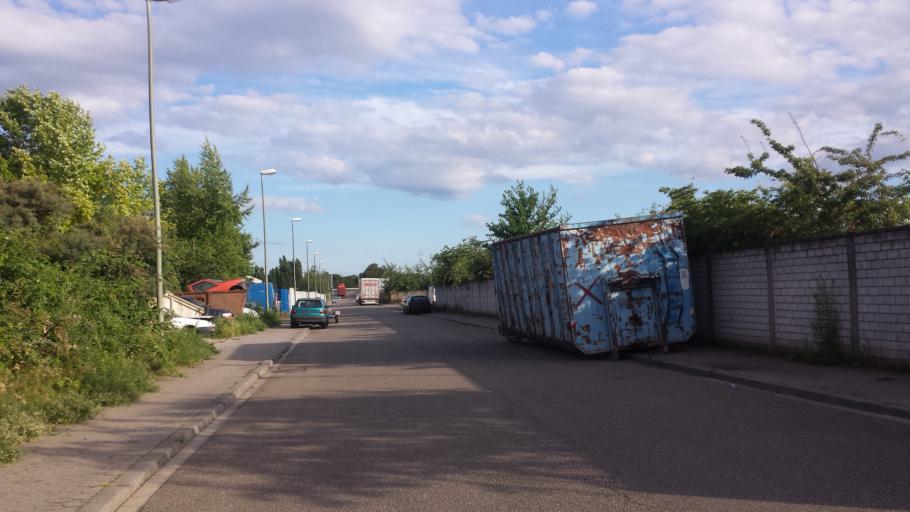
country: DE
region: Rheinland-Pfalz
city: Gartenstadt
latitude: 49.4538
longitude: 8.4163
